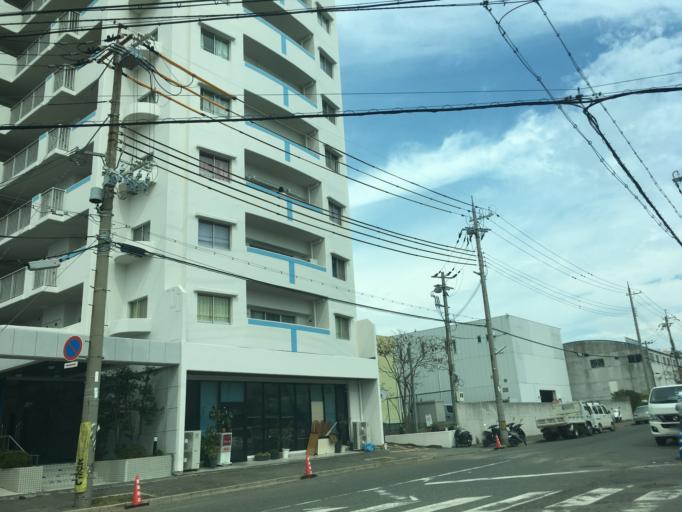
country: JP
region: Hyogo
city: Ashiya
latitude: 34.7157
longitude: 135.2961
